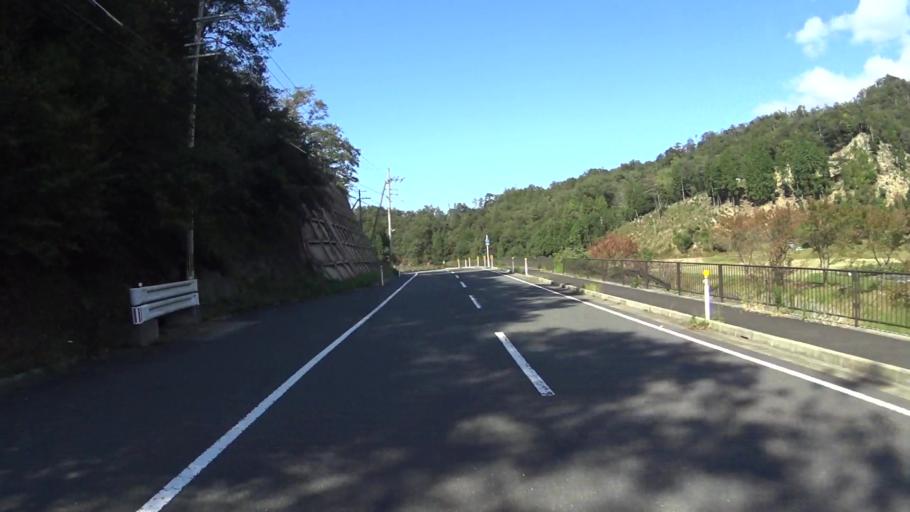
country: JP
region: Hyogo
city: Toyooka
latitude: 35.5634
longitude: 134.9781
